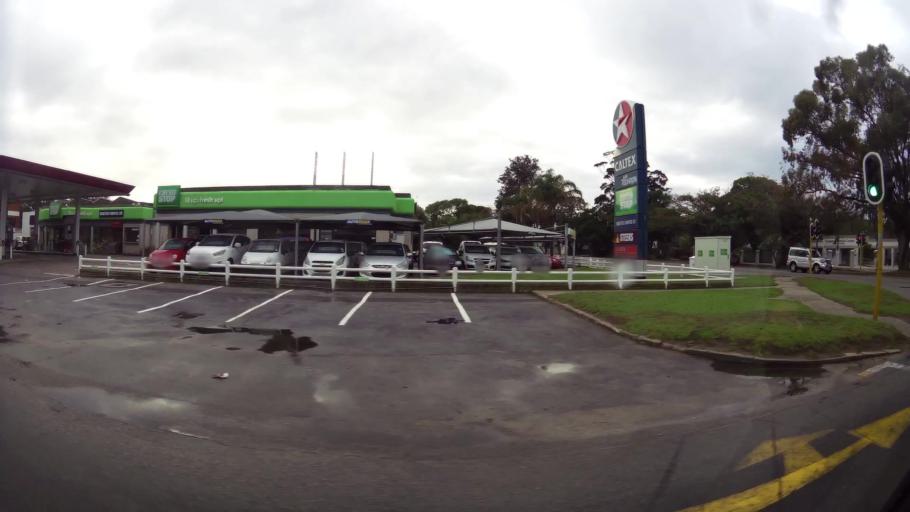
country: ZA
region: Eastern Cape
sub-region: Nelson Mandela Bay Metropolitan Municipality
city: Port Elizabeth
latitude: -33.9777
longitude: 25.5863
